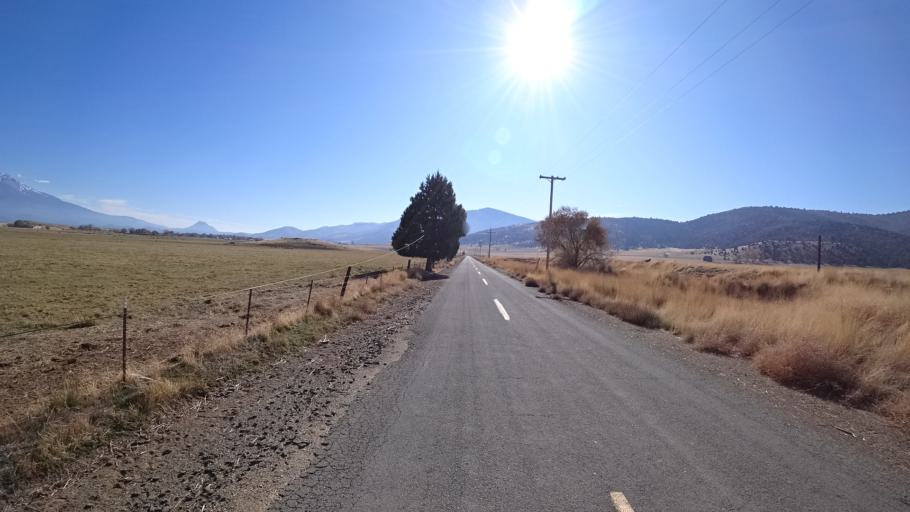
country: US
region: California
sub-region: Siskiyou County
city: Weed
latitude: 41.5334
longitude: -122.5352
